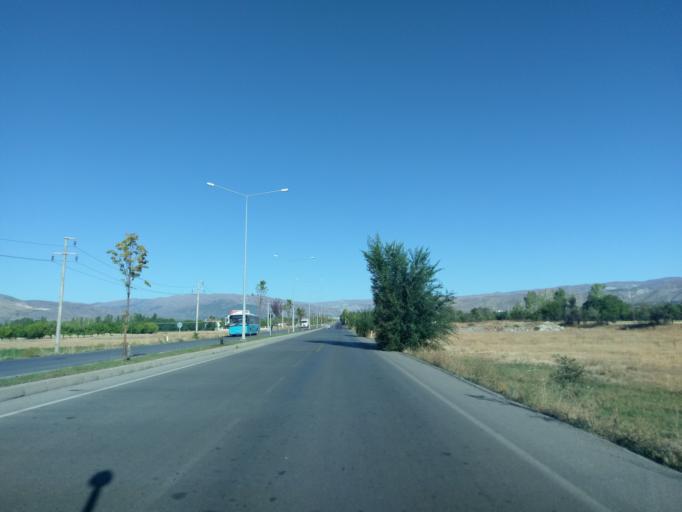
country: TR
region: Erzincan
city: Erzincan
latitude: 39.7666
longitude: 39.4323
